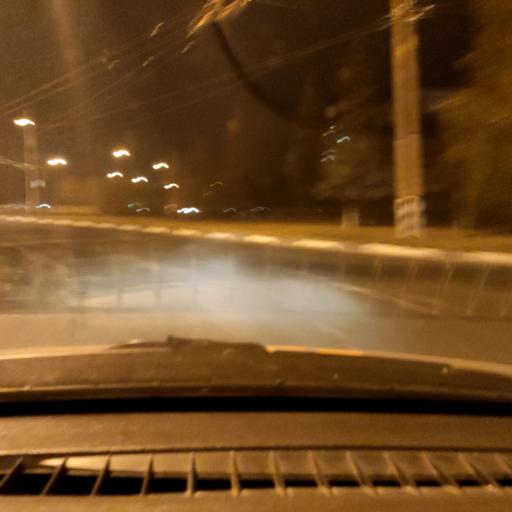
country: RU
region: Samara
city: Tol'yatti
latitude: 53.5276
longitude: 49.2979
